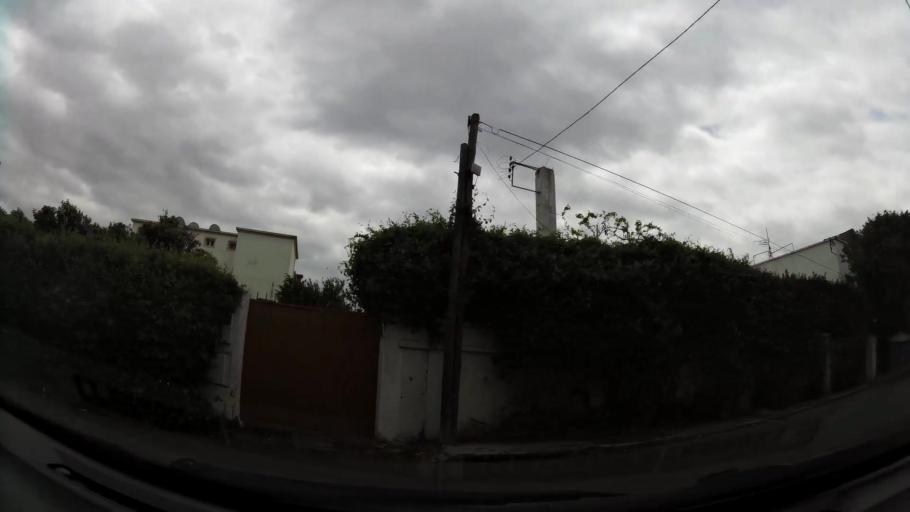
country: MA
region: Grand Casablanca
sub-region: Casablanca
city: Casablanca
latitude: 33.5617
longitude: -7.6338
